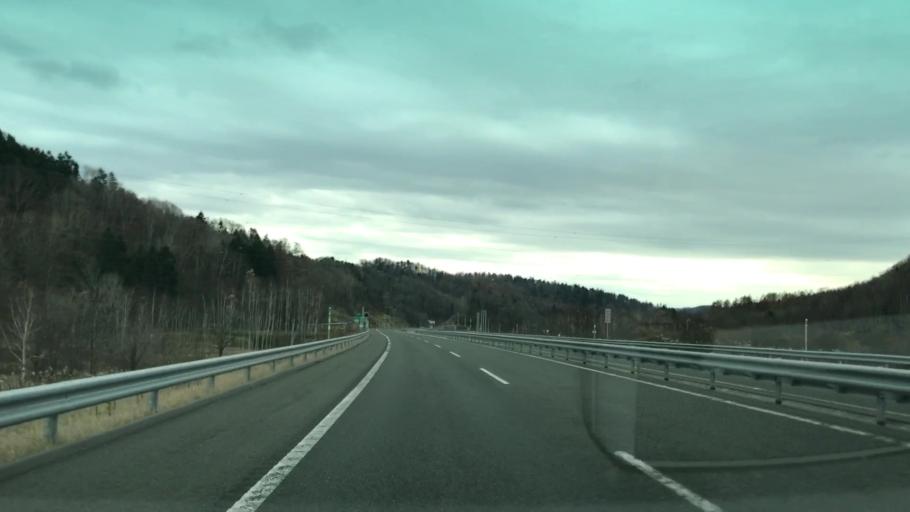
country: JP
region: Hokkaido
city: Shimo-furano
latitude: 42.9303
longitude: 142.2046
